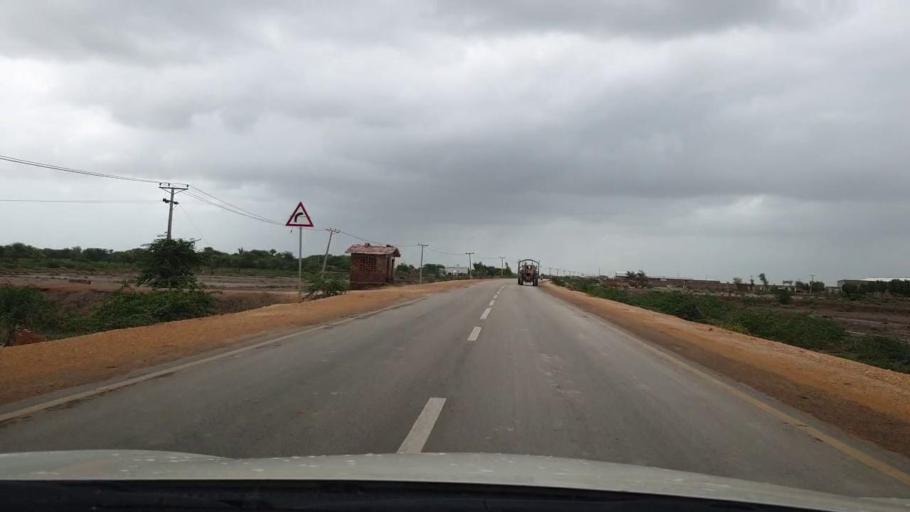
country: PK
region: Sindh
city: Badin
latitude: 24.6542
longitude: 68.7616
